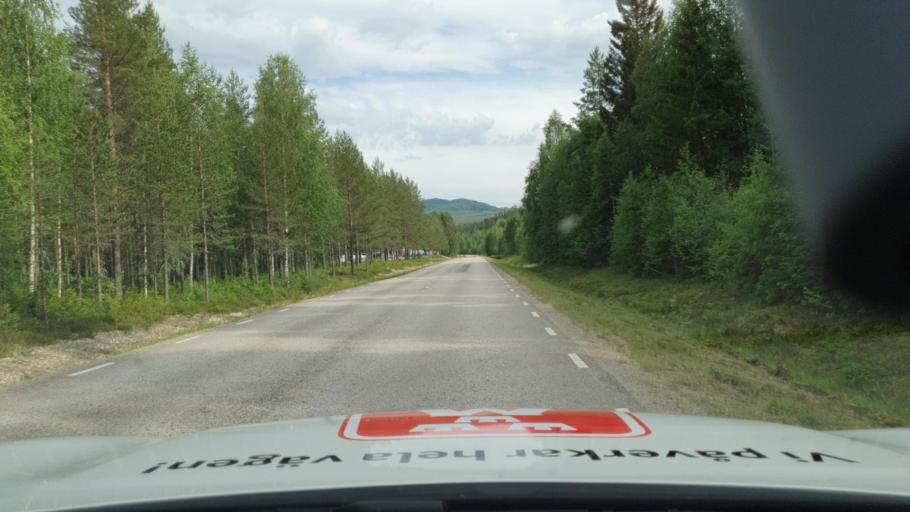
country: NO
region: Hedmark
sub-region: Trysil
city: Innbygda
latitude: 60.9088
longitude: 12.5593
